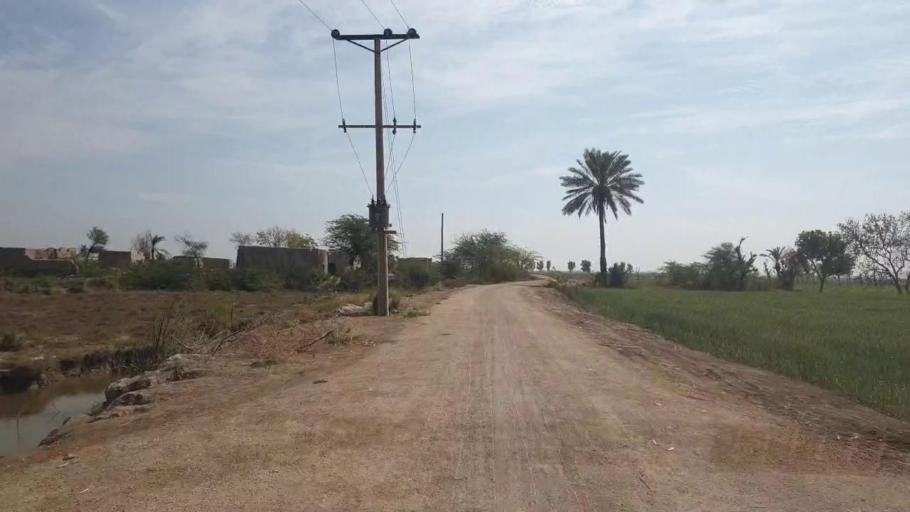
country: PK
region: Sindh
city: Samaro
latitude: 25.3617
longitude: 69.2641
